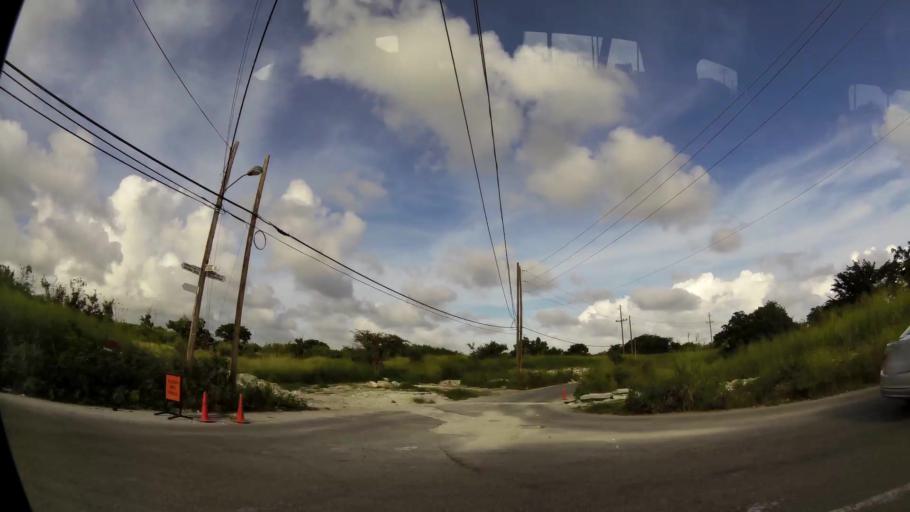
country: BB
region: Christ Church
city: Oistins
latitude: 13.0830
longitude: -59.5567
